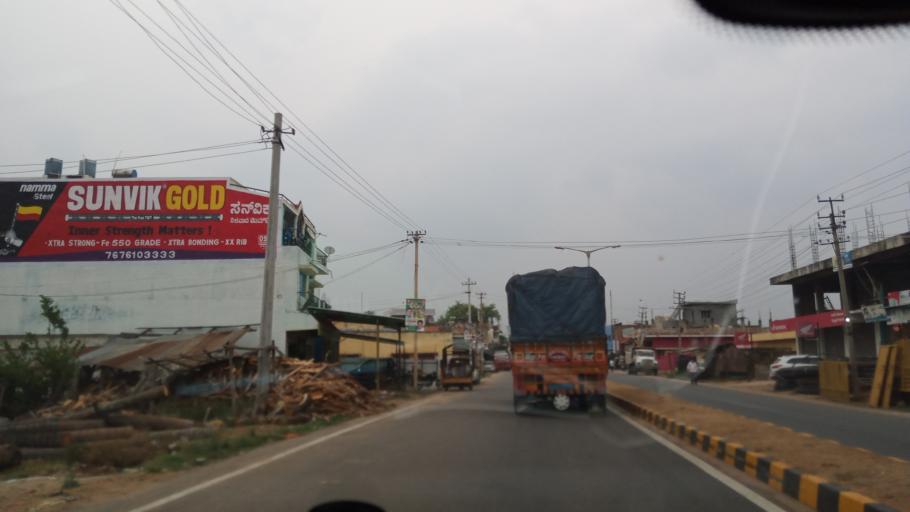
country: IN
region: Karnataka
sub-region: Mandya
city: Nagamangala
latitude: 12.8170
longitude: 76.7568
